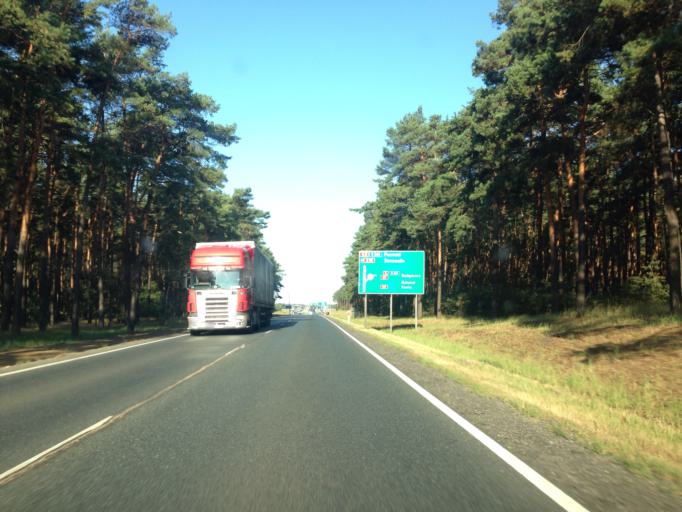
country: PL
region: Kujawsko-Pomorskie
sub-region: Bydgoszcz
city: Bydgoszcz
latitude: 53.0505
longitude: 18.0133
